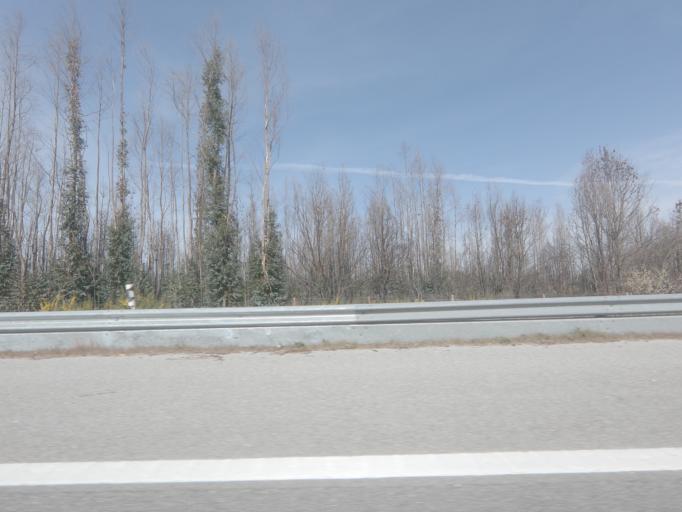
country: PT
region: Viseu
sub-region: Oliveira de Frades
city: Oliveira de Frades
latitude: 40.6860
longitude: -8.2096
